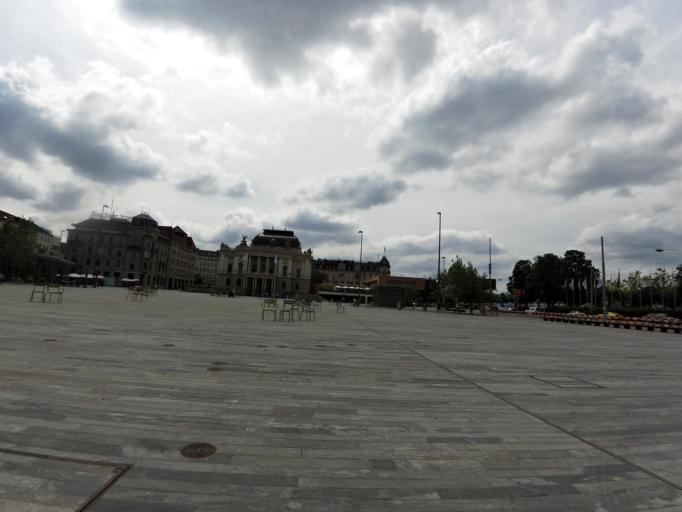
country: CH
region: Zurich
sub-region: Bezirk Zuerich
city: Zurich
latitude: 47.3662
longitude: 8.5457
